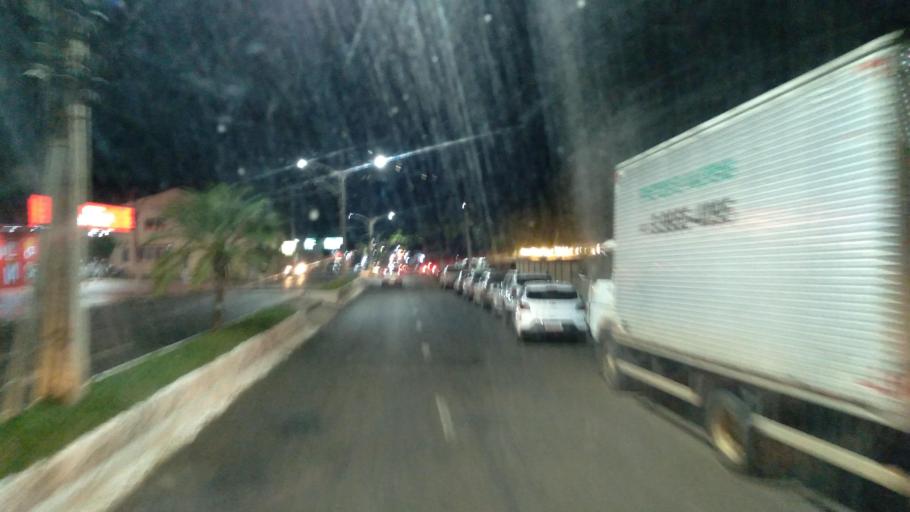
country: BR
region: Goias
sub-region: Mineiros
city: Mineiros
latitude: -17.5645
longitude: -52.5568
